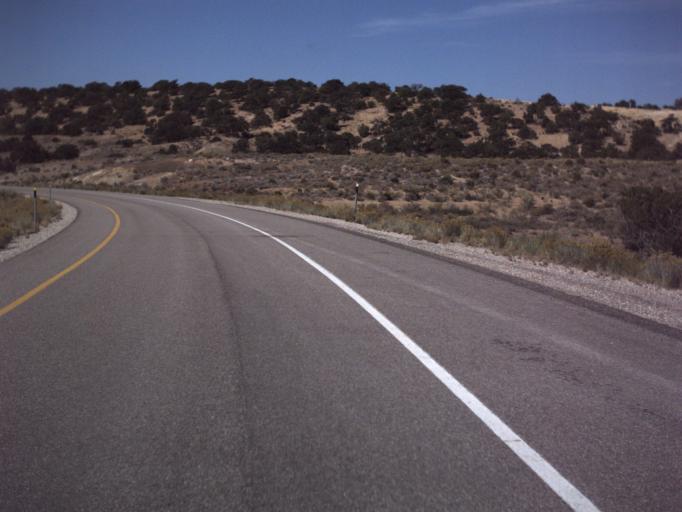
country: US
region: Utah
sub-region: Emery County
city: Ferron
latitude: 38.8566
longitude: -110.9152
